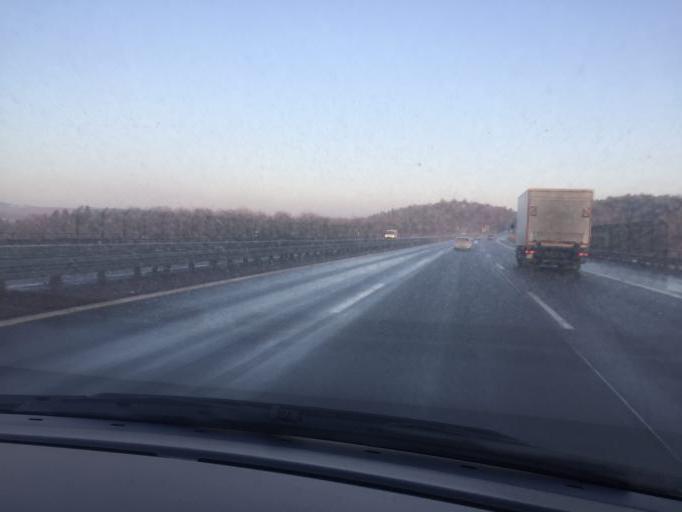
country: DE
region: Baden-Wuerttemberg
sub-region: Freiburg Region
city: Engen
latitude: 47.8685
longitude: 8.7801
